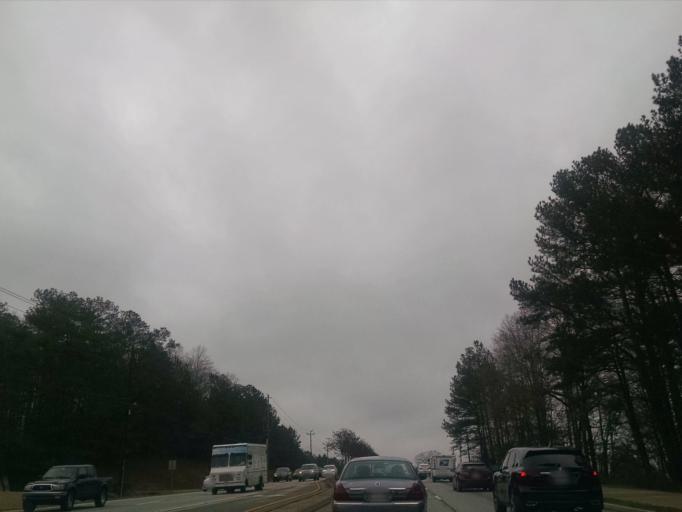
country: US
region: Georgia
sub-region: Gwinnett County
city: Suwanee
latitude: 34.0599
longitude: -84.0692
